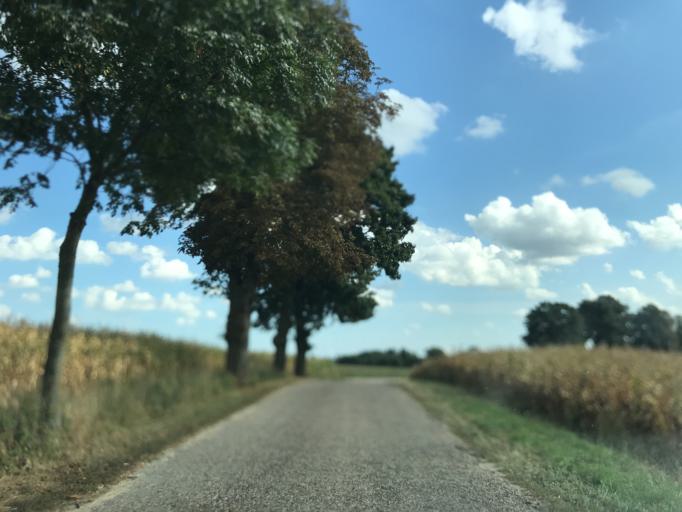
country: PL
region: Kujawsko-Pomorskie
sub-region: Powiat brodnicki
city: Brzozie
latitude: 53.3553
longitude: 19.6757
